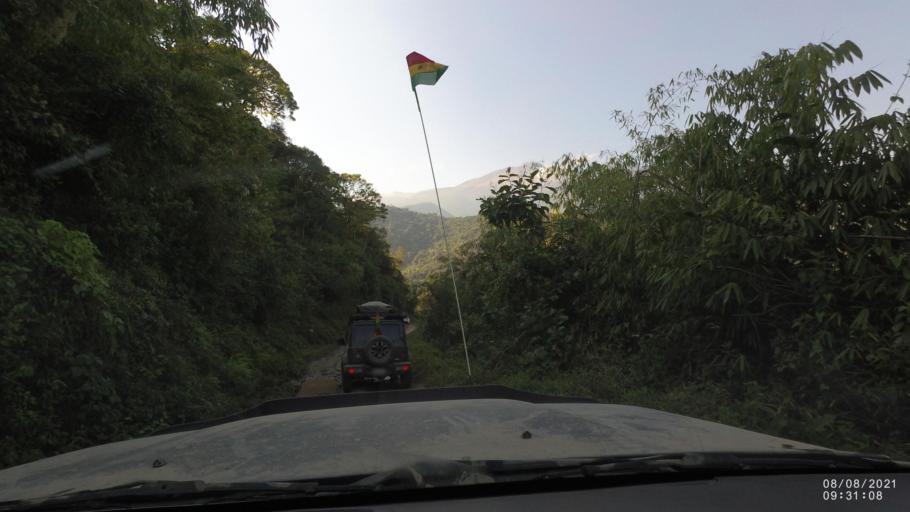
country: BO
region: La Paz
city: Quime
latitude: -16.5879
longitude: -66.7086
